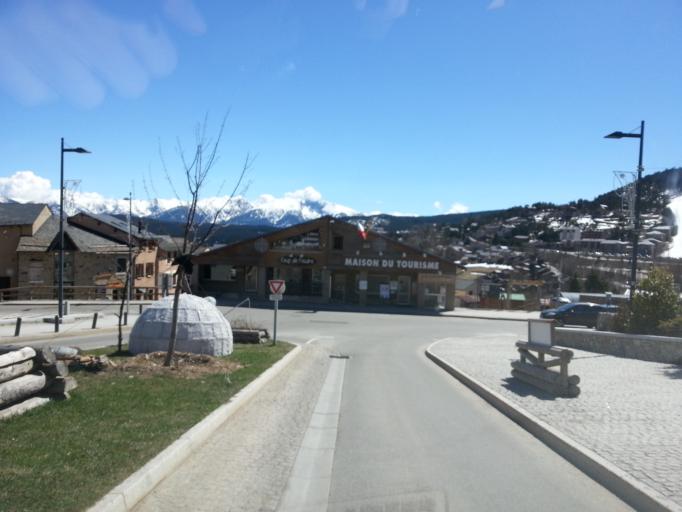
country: ES
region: Catalonia
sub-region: Provincia de Girona
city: Llivia
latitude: 42.5779
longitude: 2.0725
